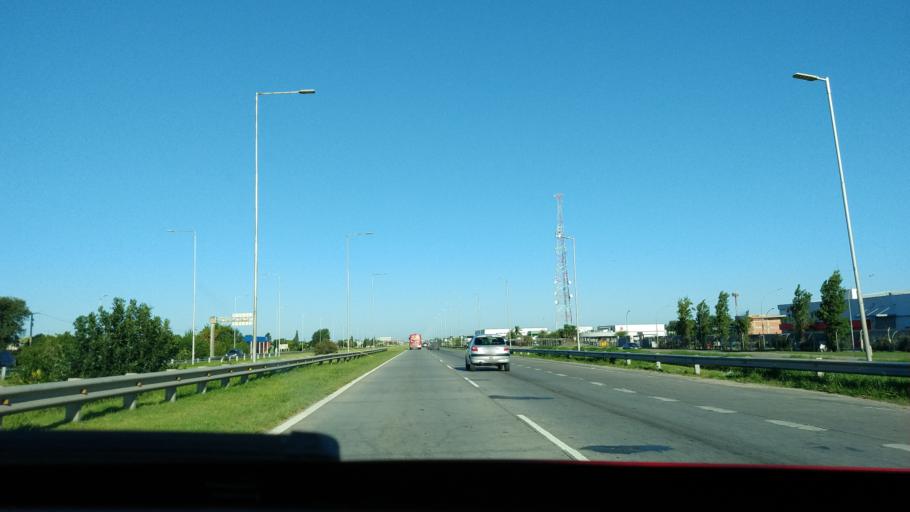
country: AR
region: Cordoba
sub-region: Departamento de Capital
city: Cordoba
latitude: -31.3583
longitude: -64.1729
